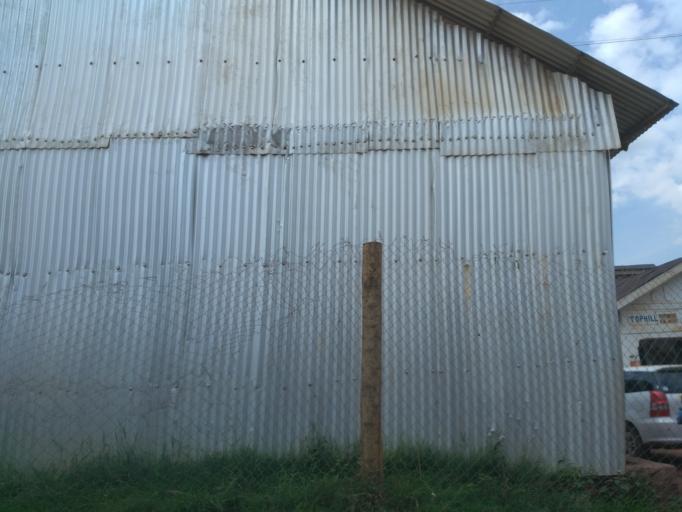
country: UG
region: Central Region
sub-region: Wakiso District
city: Bweyogerere
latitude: 0.4649
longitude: 32.6246
